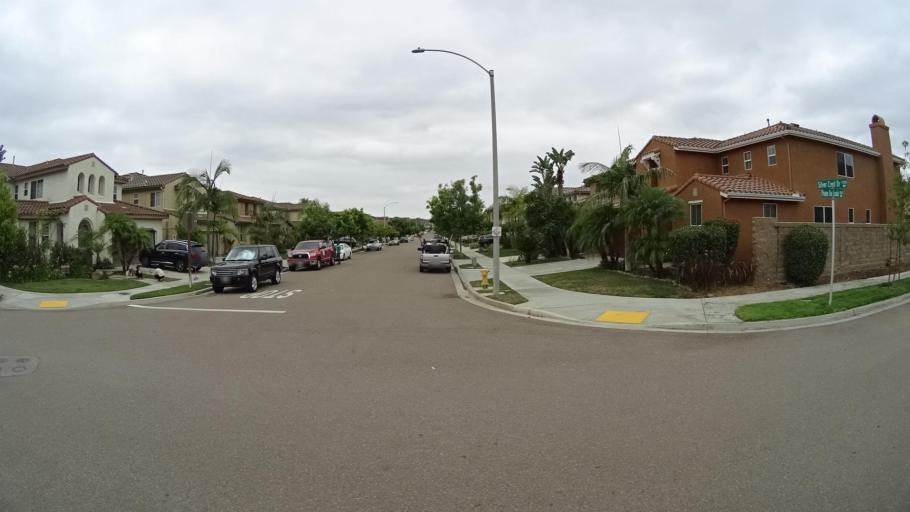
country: US
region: California
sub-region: San Diego County
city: Fairbanks Ranch
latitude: 33.0274
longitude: -117.1131
